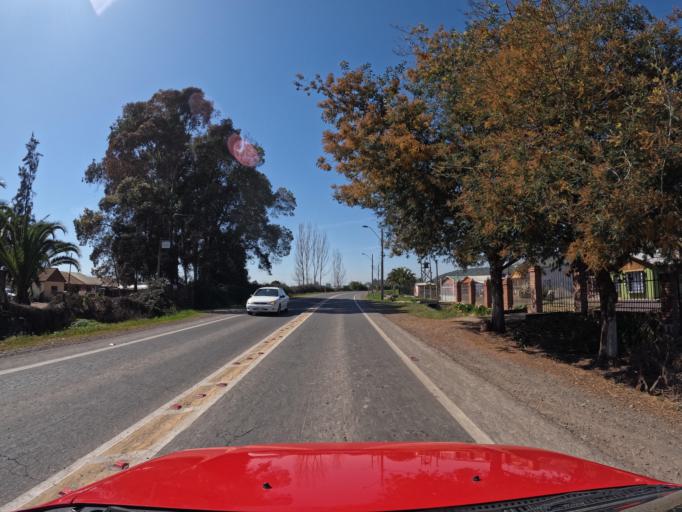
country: CL
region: Maule
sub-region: Provincia de Curico
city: Rauco
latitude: -35.0075
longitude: -71.4081
